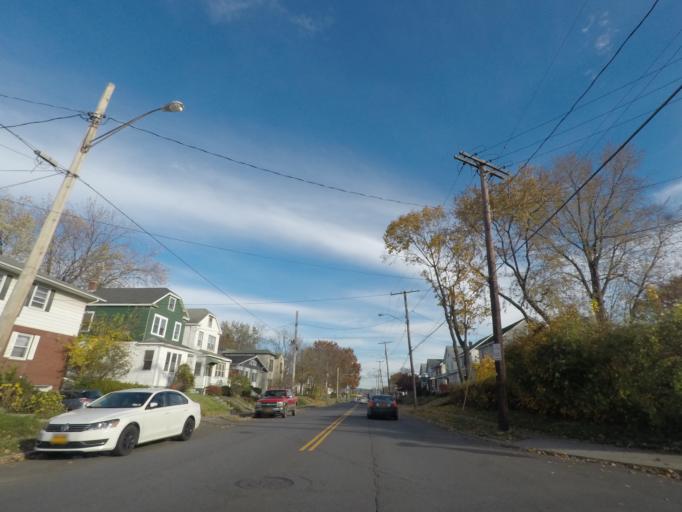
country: US
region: New York
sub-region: Albany County
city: Albany
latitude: 42.6363
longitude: -73.7803
